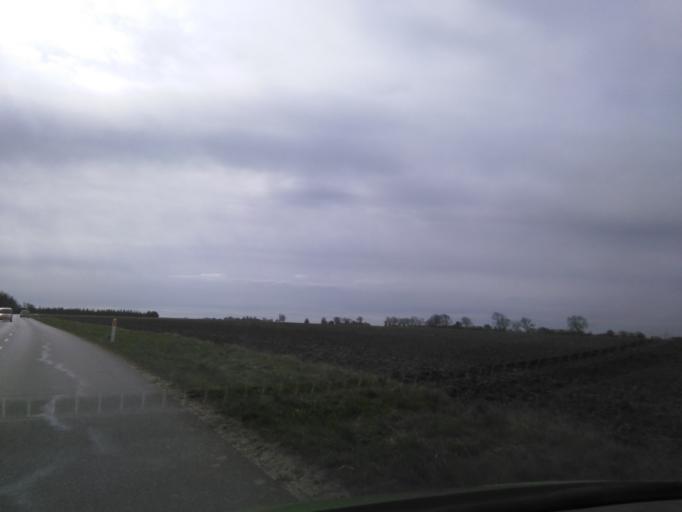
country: DK
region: Central Jutland
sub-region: Odder Kommune
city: Odder
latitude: 55.9608
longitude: 10.2340
